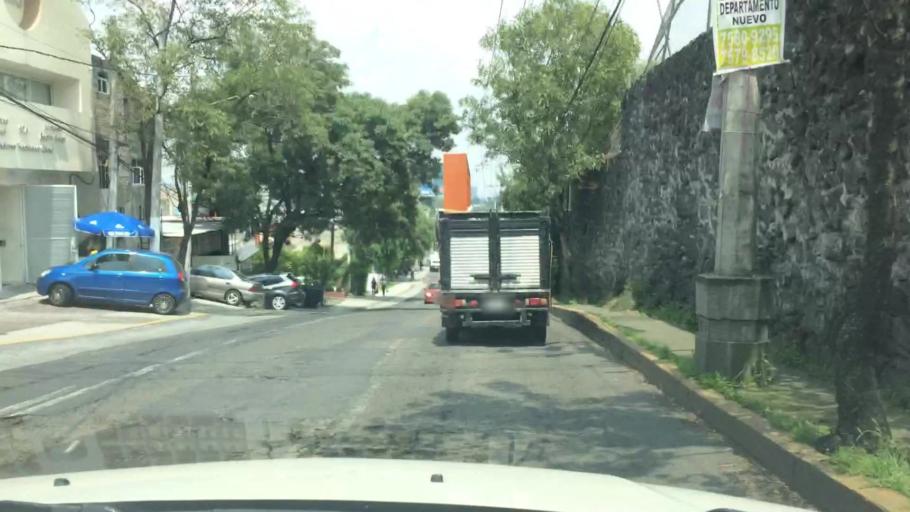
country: MX
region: Mexico City
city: Magdalena Contreras
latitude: 19.3025
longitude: -99.2210
